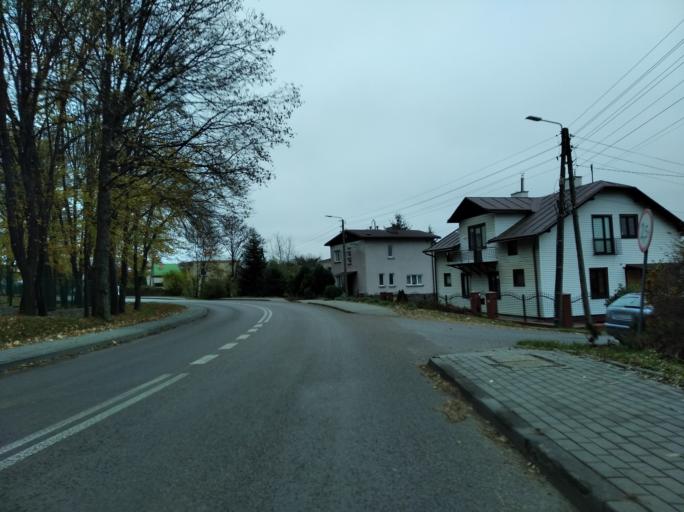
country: PL
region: Subcarpathian Voivodeship
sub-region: Krosno
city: Krosno
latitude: 49.7007
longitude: 21.7622
